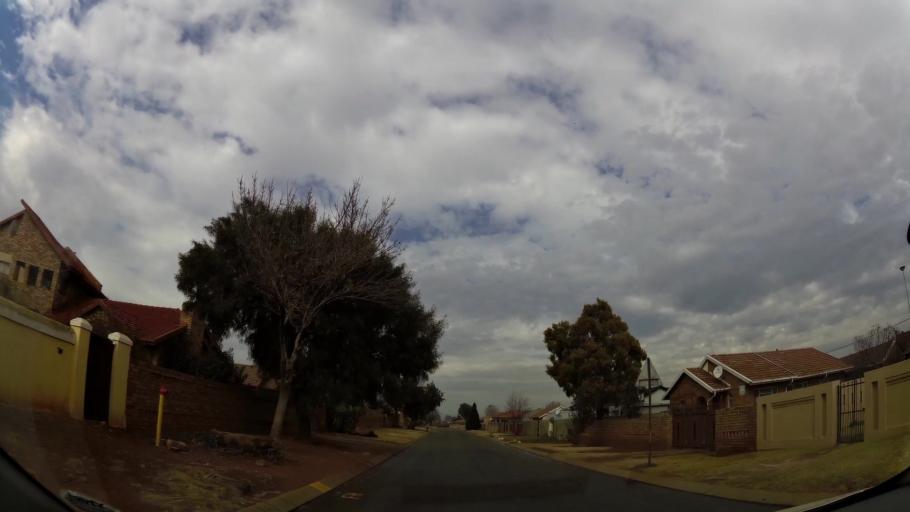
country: ZA
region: Gauteng
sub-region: Ekurhuleni Metropolitan Municipality
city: Germiston
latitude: -26.3301
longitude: 28.1783
